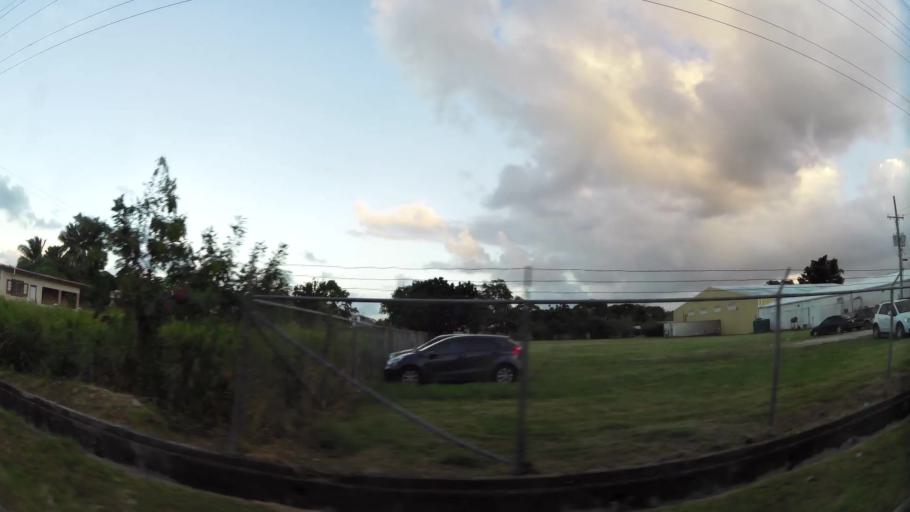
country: AG
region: Saint John
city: Saint John's
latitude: 17.1262
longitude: -61.8393
